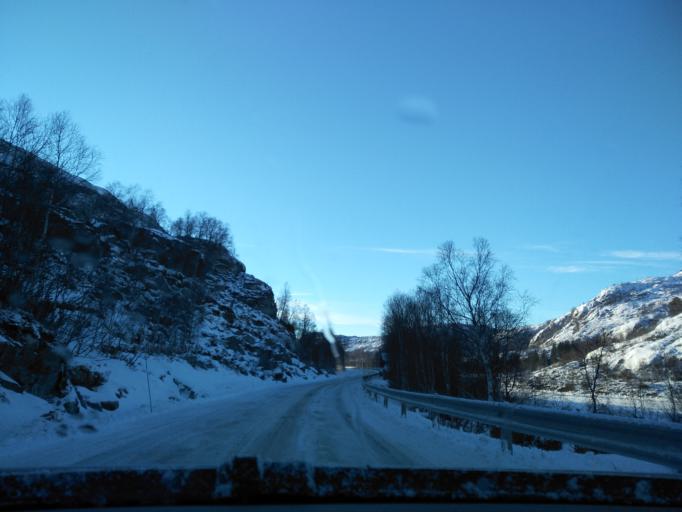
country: NO
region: Vest-Agder
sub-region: Sirdal
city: Tonstad
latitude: 59.0104
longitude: 6.9353
